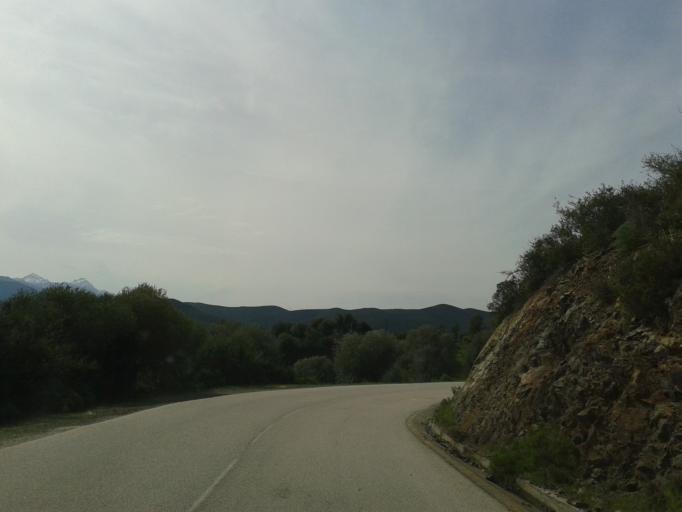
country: FR
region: Corsica
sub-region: Departement de la Haute-Corse
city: Monticello
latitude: 42.6472
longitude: 9.1011
